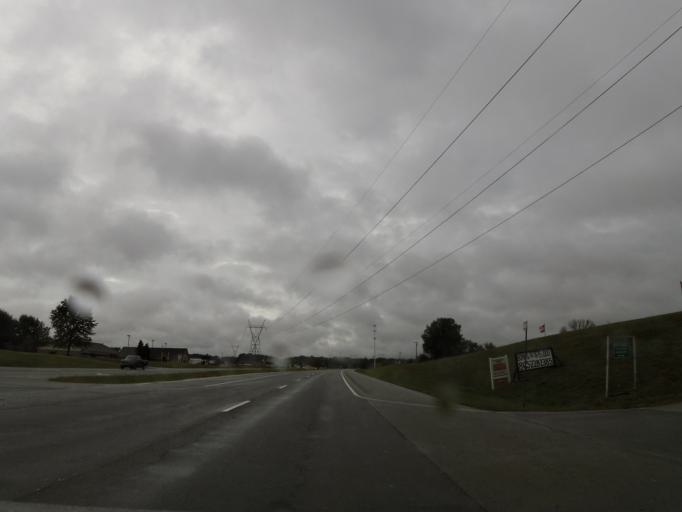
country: US
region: Tennessee
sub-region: Blount County
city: Maryville
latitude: 35.7549
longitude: -84.0176
